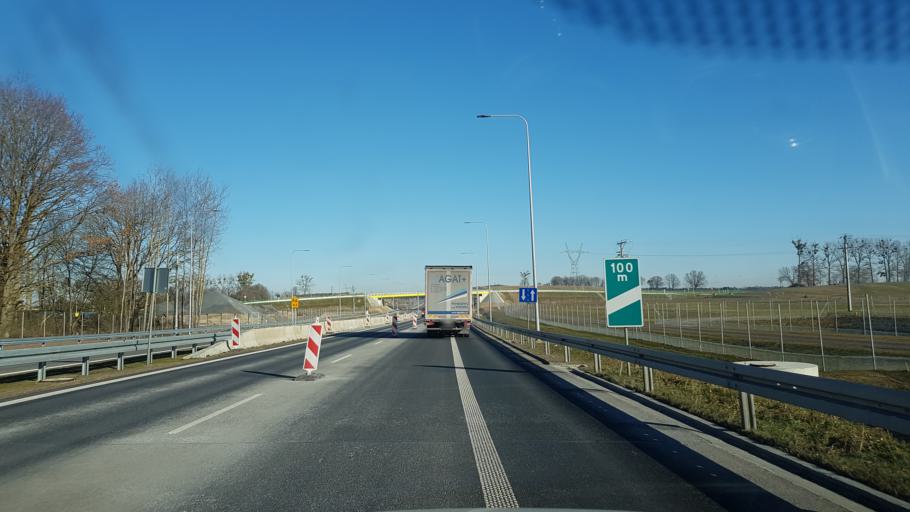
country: PL
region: West Pomeranian Voivodeship
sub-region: Powiat goleniowski
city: Przybiernow
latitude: 53.7859
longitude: 14.7770
